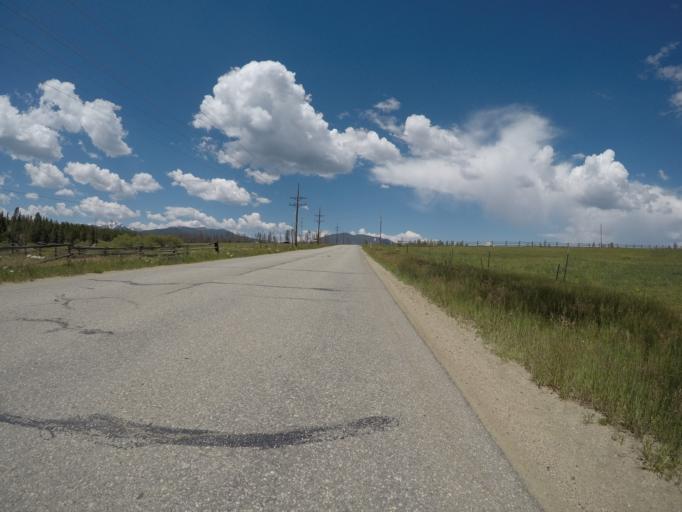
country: US
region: Colorado
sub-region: Grand County
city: Fraser
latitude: 39.9554
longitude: -105.8304
